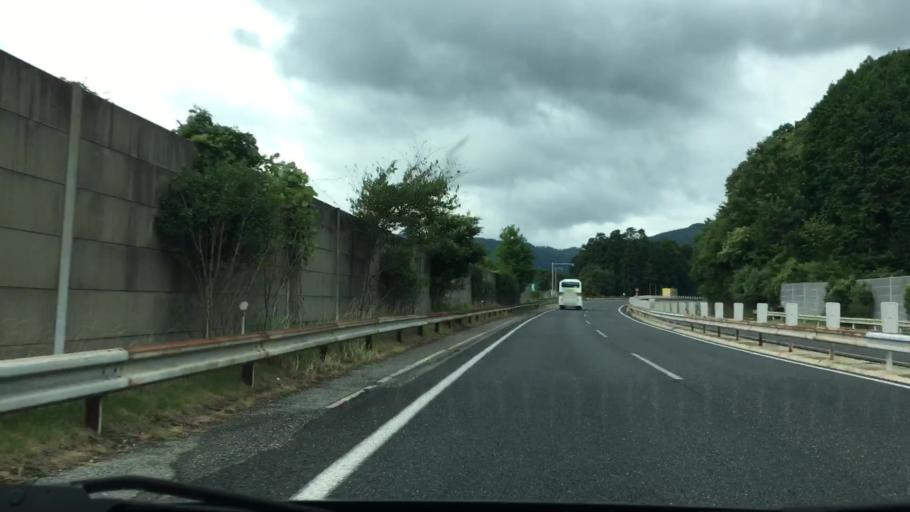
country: JP
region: Okayama
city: Takahashi
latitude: 34.9947
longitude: 133.7234
